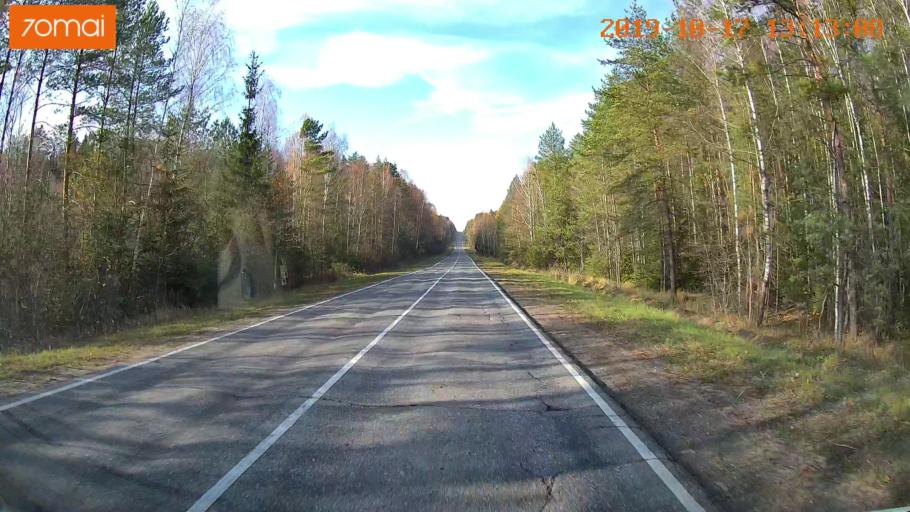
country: RU
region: Rjazan
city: Gus'-Zheleznyy
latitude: 55.0424
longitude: 41.1978
